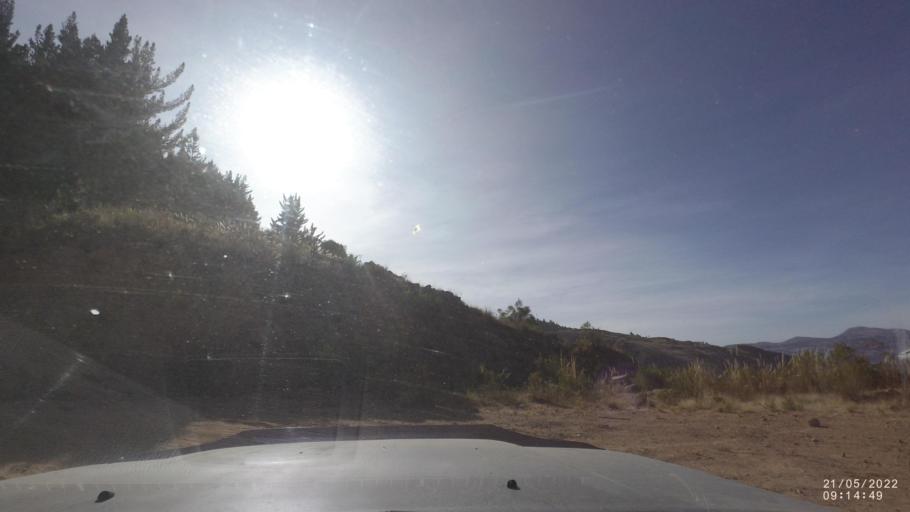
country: BO
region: Cochabamba
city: Cochabamba
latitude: -17.3655
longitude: -66.0282
